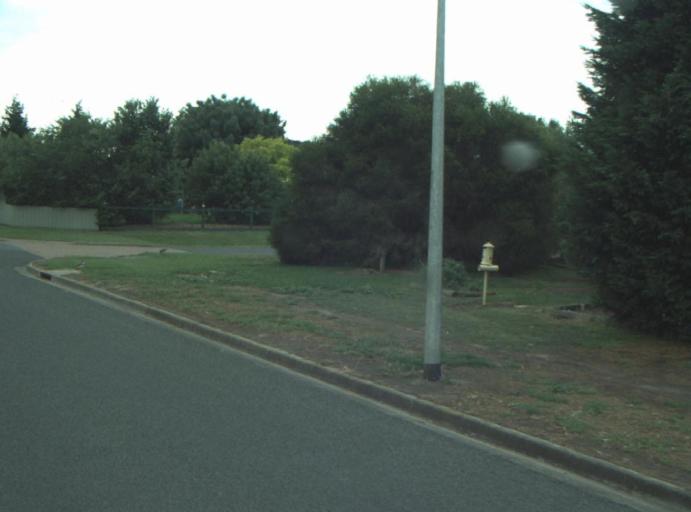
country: AU
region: Victoria
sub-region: Greater Geelong
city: Breakwater
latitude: -38.1931
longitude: 144.3873
